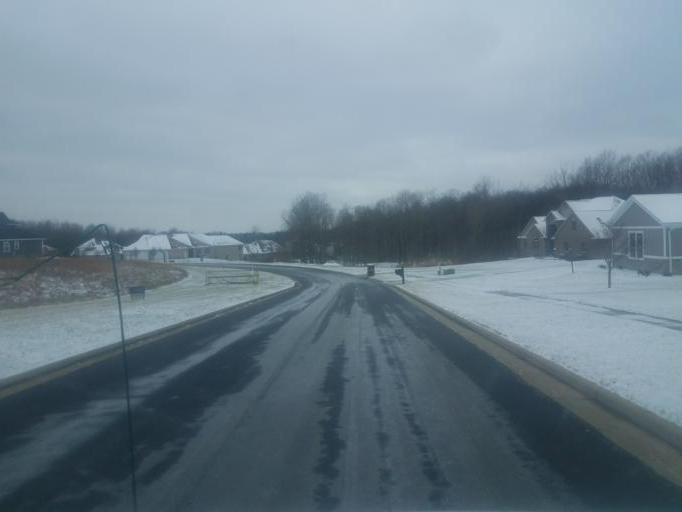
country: US
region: Ohio
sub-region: Richland County
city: Ontario
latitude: 40.7562
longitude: -82.6534
